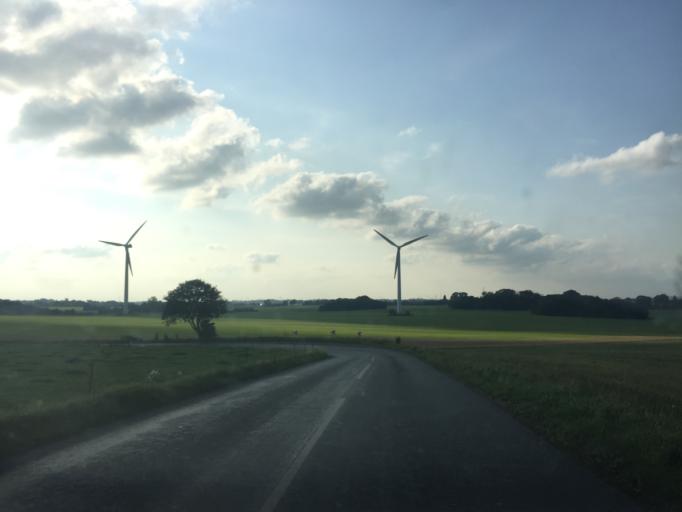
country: DK
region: Zealand
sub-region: Kalundborg Kommune
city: Svebolle
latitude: 55.6430
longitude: 11.2258
